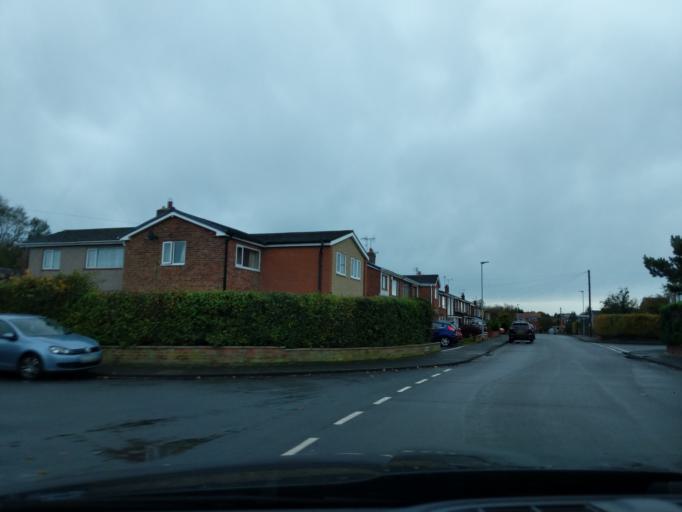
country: GB
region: England
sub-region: Northumberland
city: Morpeth
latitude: 55.1561
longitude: -1.6793
